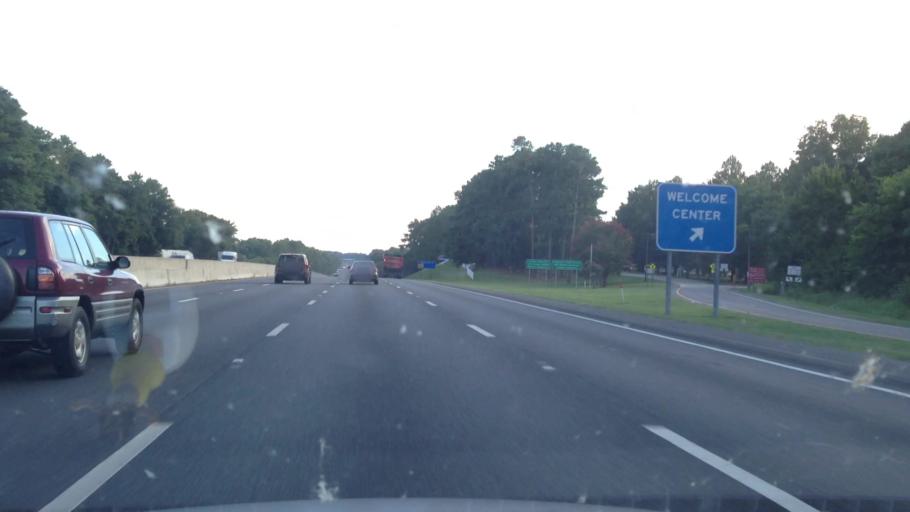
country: US
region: North Carolina
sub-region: Mecklenburg County
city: Pineville
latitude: 35.0822
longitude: -80.9407
